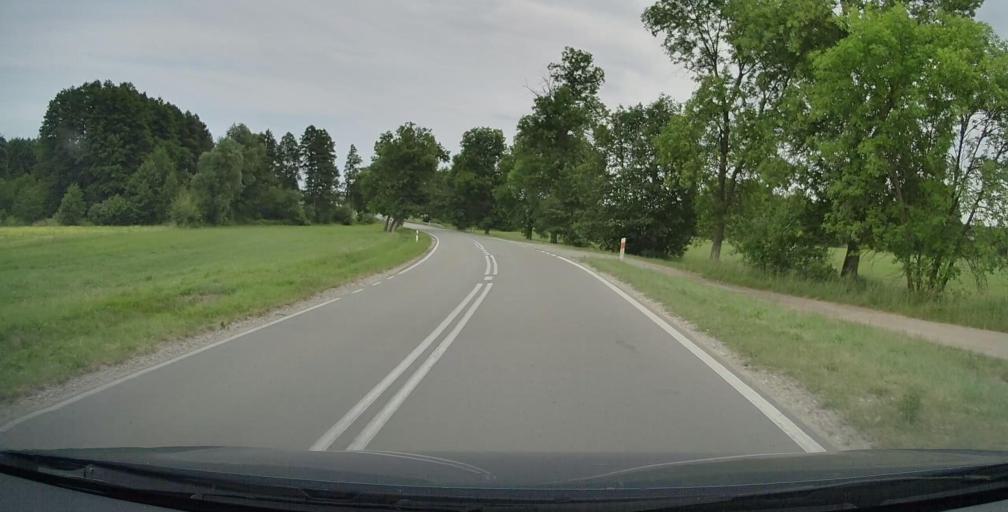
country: PL
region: Masovian Voivodeship
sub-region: Powiat losicki
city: Sarnaki
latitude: 52.3071
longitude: 22.9454
